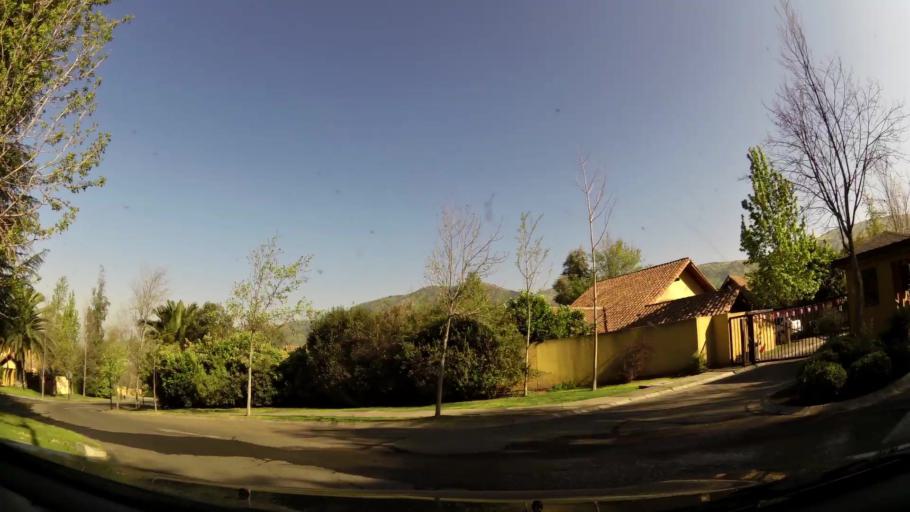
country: CL
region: Santiago Metropolitan
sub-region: Provincia de Chacabuco
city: Chicureo Abajo
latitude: -33.3452
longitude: -70.6634
